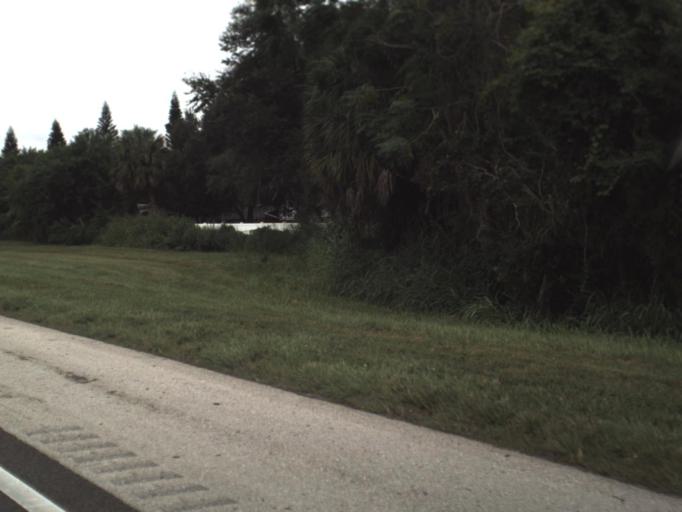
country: US
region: Florida
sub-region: Manatee County
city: Ellenton
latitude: 27.5031
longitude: -82.4819
